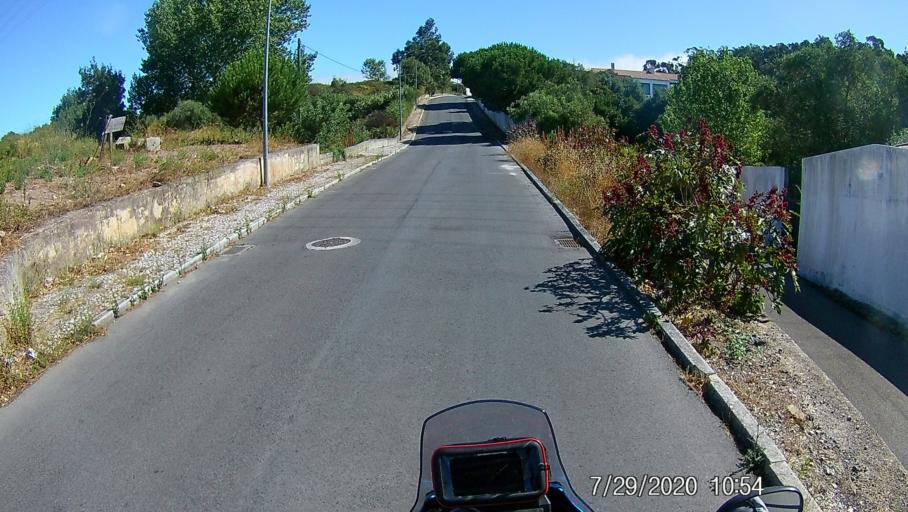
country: PT
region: Lisbon
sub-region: Sintra
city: Rio de Mouro
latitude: 38.7527
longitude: -9.3658
